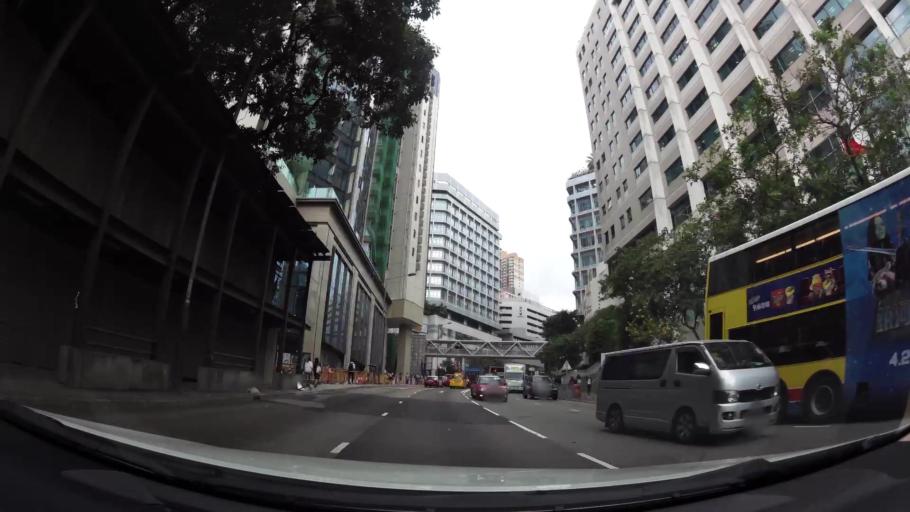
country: HK
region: Kowloon City
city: Kowloon
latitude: 22.3167
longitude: 114.1804
